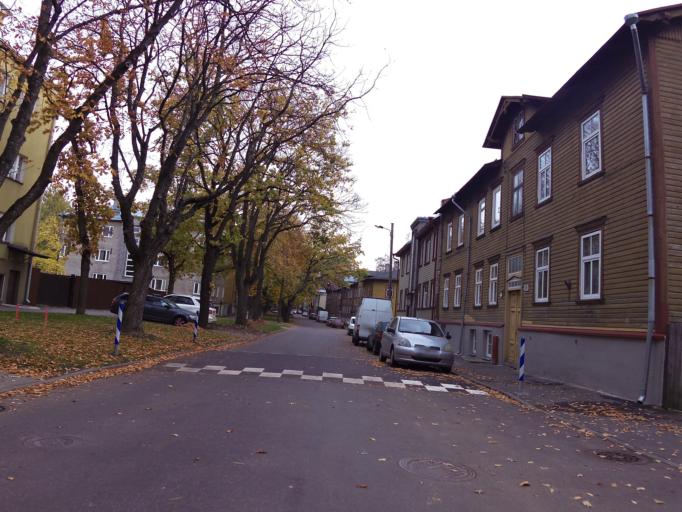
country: EE
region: Harju
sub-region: Tallinna linn
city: Tallinn
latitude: 59.4397
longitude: 24.7204
